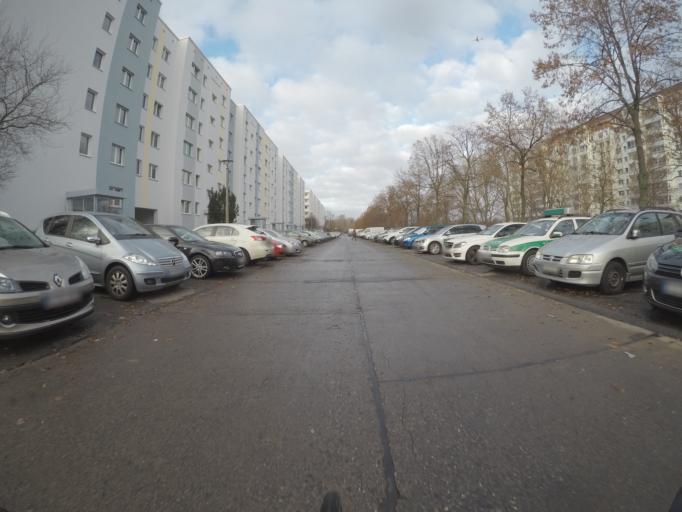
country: DE
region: Berlin
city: Neu-Hohenschoenhausen
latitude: 52.5708
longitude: 13.4961
